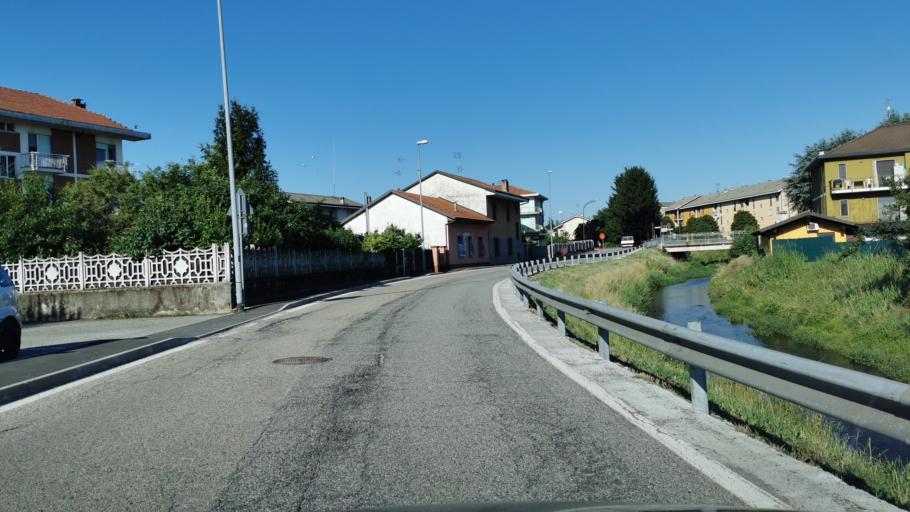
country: IT
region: Piedmont
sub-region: Provincia di Torino
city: Brandizzo
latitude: 45.1819
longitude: 7.8417
